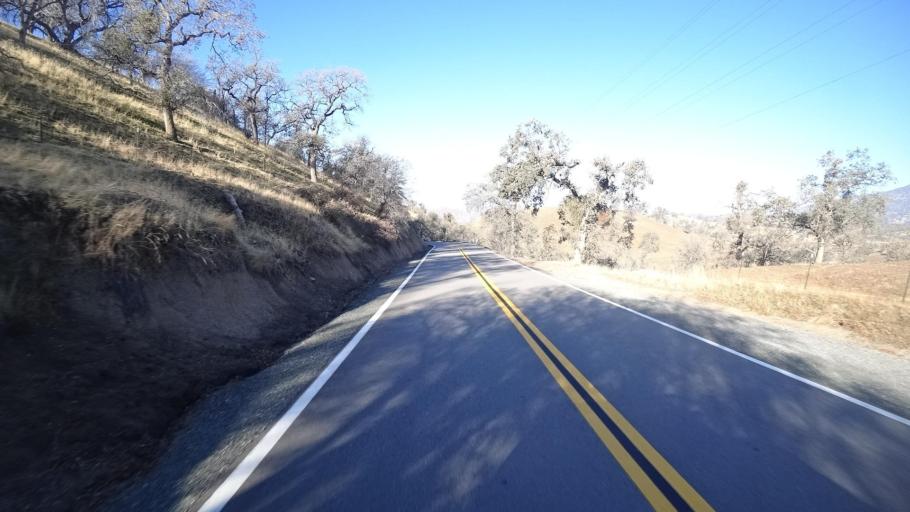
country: US
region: California
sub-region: Kern County
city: Alta Sierra
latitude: 35.7194
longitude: -118.7944
